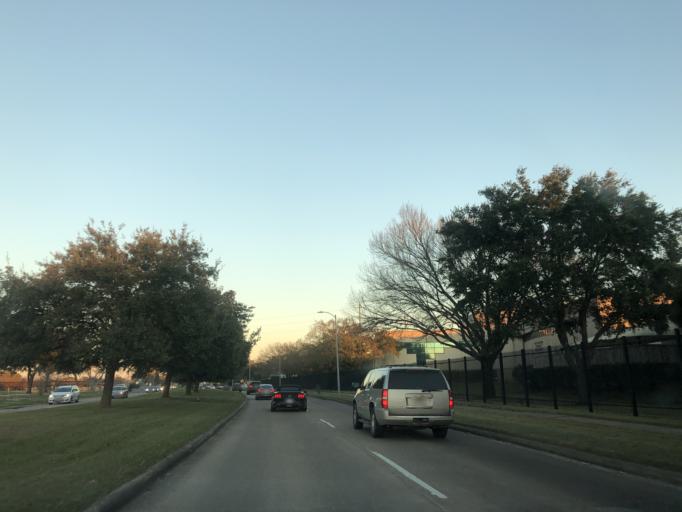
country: US
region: Texas
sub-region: Harris County
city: Bellaire
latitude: 29.6746
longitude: -95.4848
